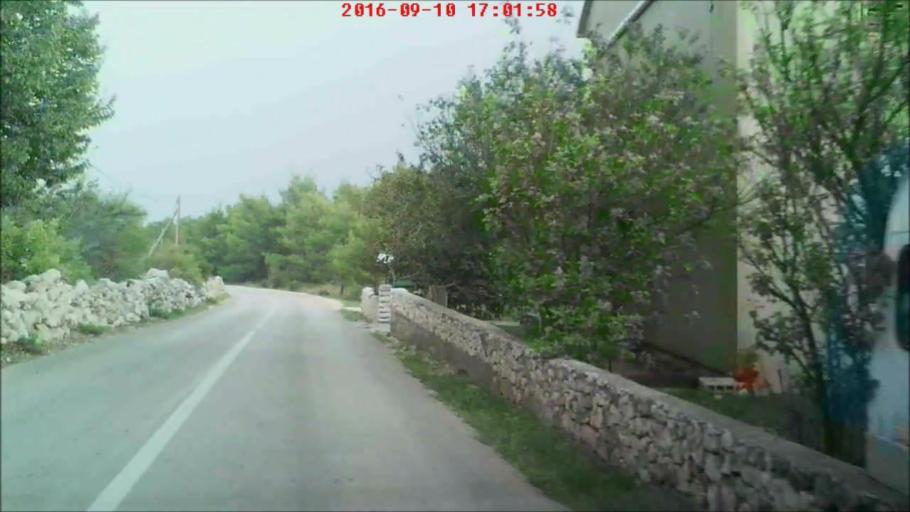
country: HR
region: Zadarska
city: Vir
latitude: 44.3056
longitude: 15.0611
